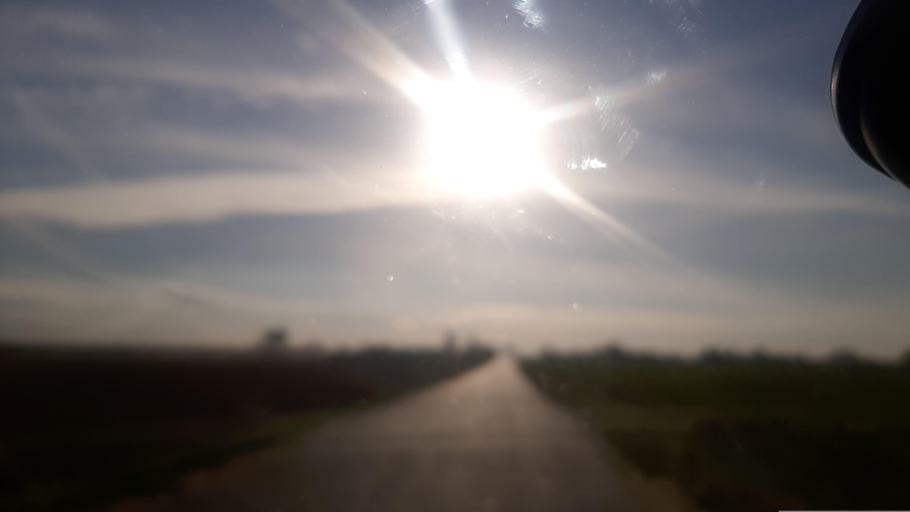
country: PL
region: Lublin Voivodeship
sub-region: Powiat lubelski
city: Garbow
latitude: 51.3915
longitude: 22.3469
